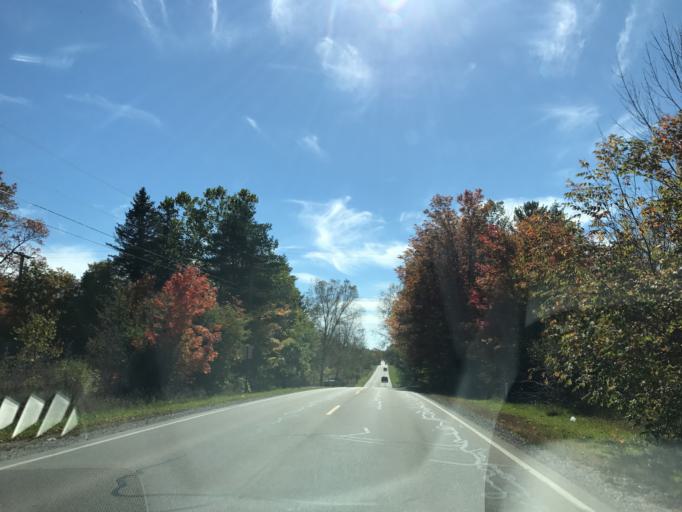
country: US
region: Michigan
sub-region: Oakland County
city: South Lyon
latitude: 42.3959
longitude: -83.6454
